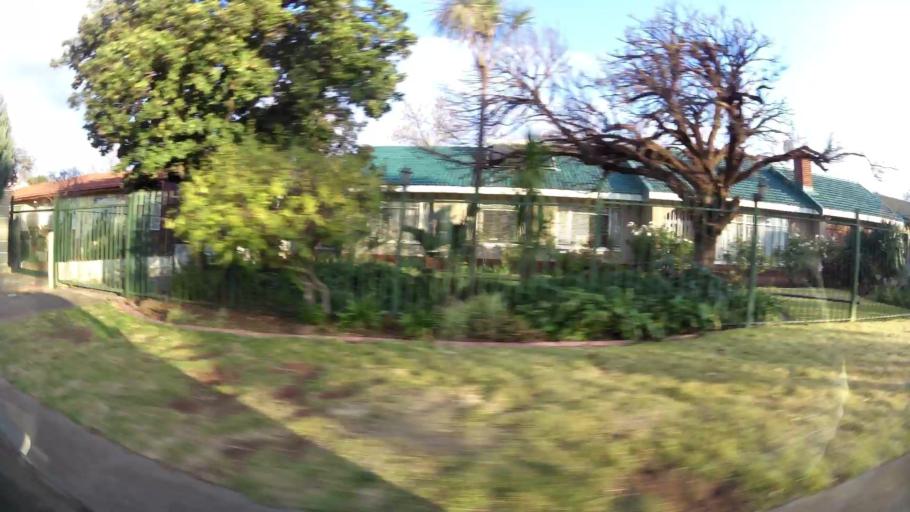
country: ZA
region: Orange Free State
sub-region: Mangaung Metropolitan Municipality
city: Bloemfontein
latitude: -29.1394
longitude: 26.1773
